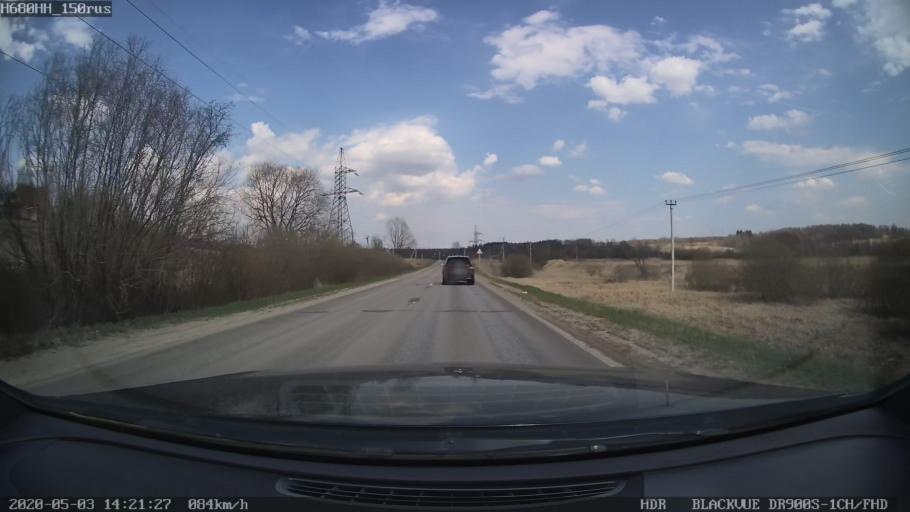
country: RU
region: Moskovskaya
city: Solnechnogorsk
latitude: 56.2551
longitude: 36.9793
